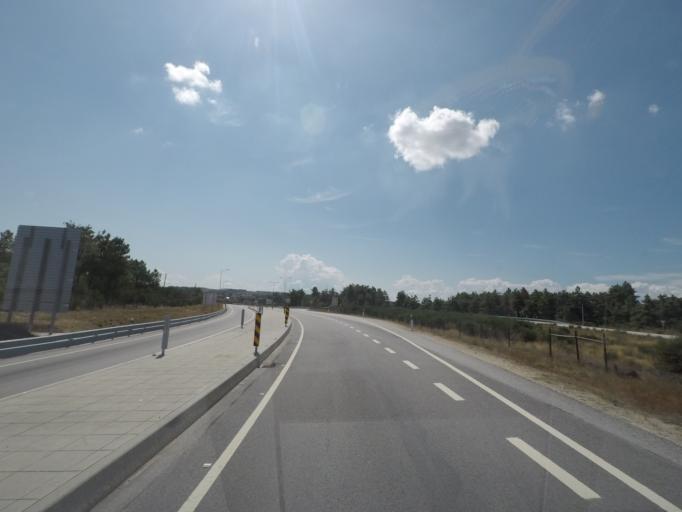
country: PT
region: Vila Real
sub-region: Murca
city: Murca
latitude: 41.3390
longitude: -7.4703
